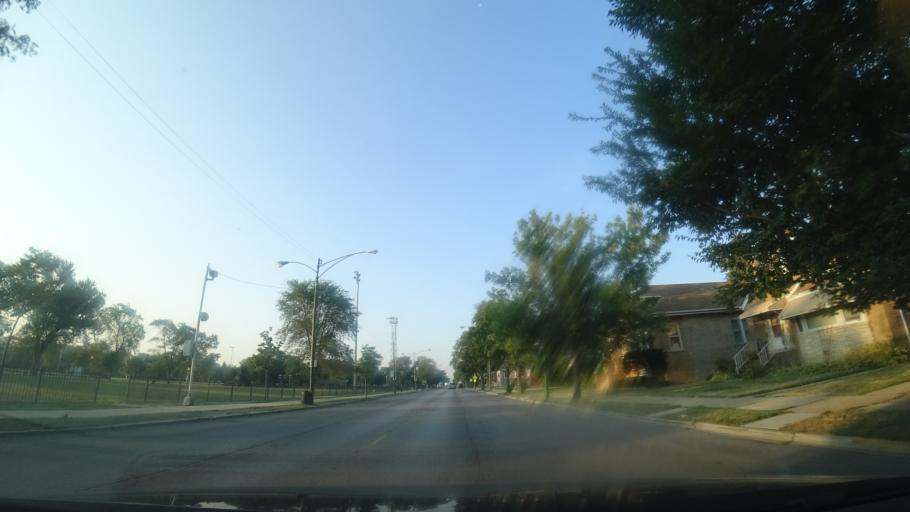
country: US
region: Illinois
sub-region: Cook County
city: Harwood Heights
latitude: 41.9559
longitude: -87.7671
